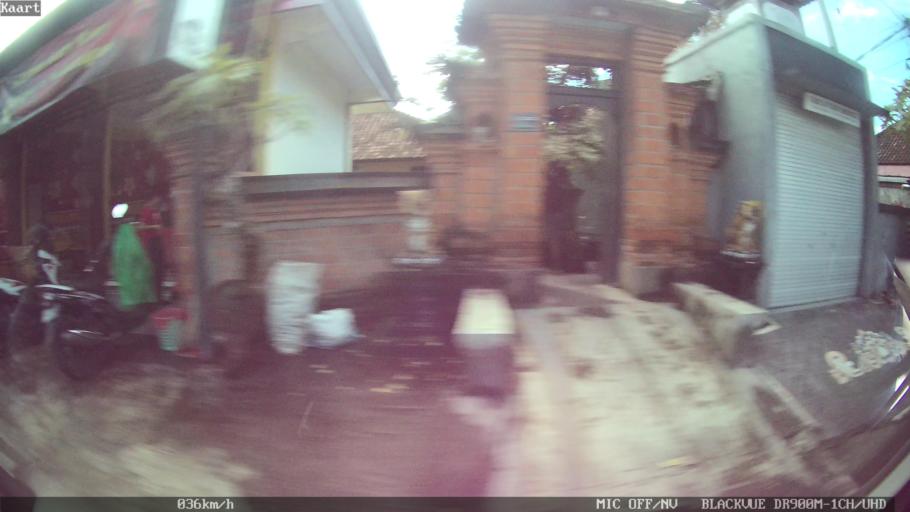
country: ID
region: Bali
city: Banjar Tebongkang
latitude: -8.5366
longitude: 115.2626
